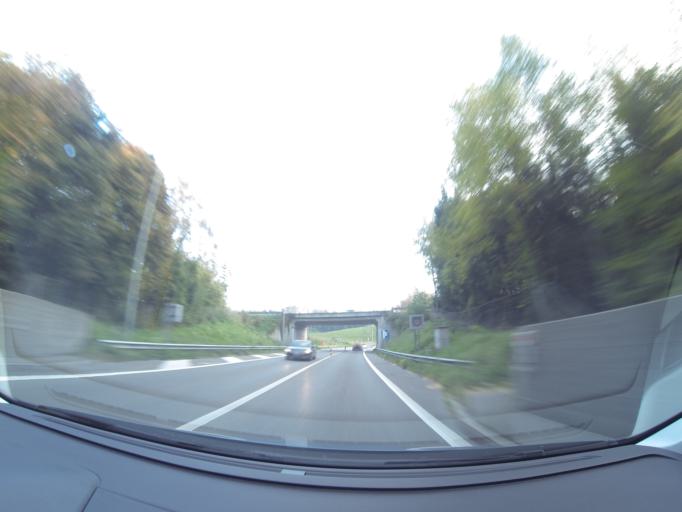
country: CH
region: Zurich
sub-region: Bezirk Hinwil
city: Rueti / Dorfzentrum, Suedl. Teil
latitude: 47.2413
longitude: 8.8629
